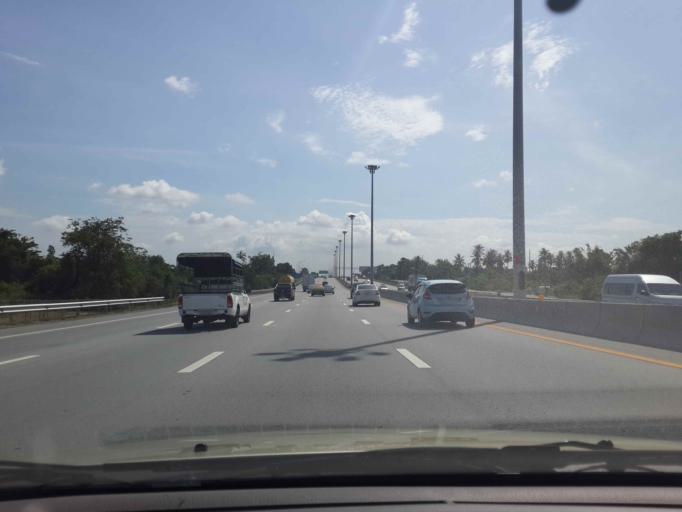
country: TH
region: Chon Buri
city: Chon Buri
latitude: 13.3137
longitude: 101.0069
